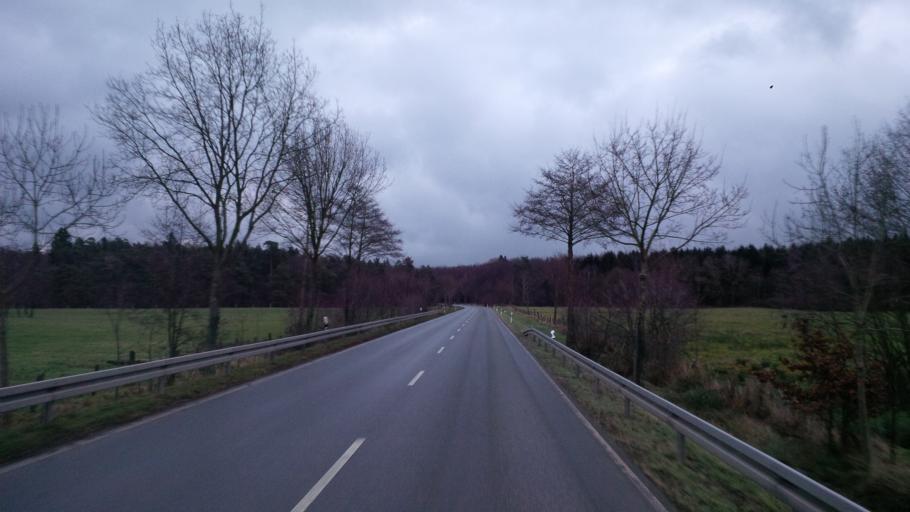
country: DE
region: Hesse
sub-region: Regierungsbezirk Darmstadt
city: Wehrheim
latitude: 50.2831
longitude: 8.5526
